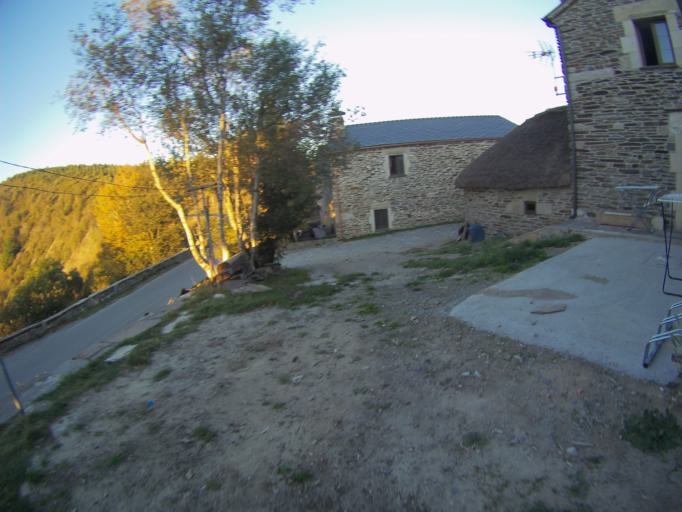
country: ES
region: Castille and Leon
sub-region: Provincia de Leon
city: Barjas
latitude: 42.7076
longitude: -7.0442
